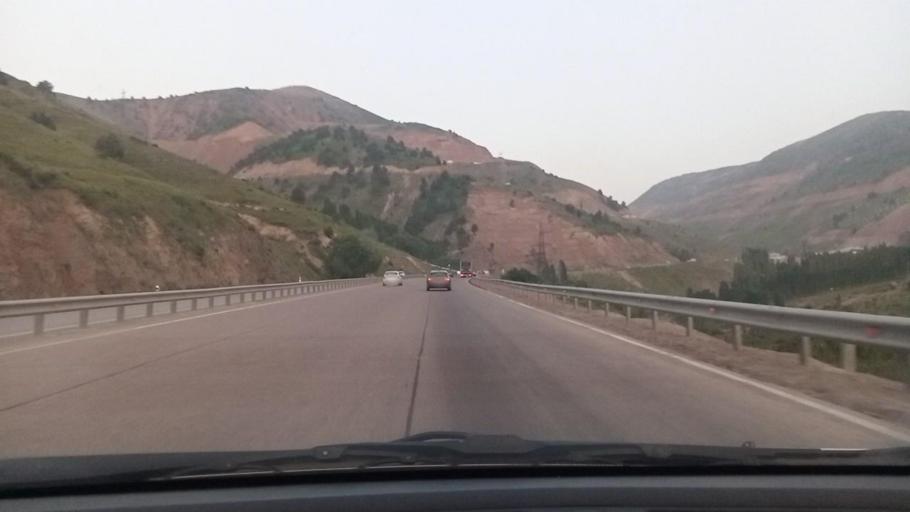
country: UZ
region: Toshkent
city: Angren
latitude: 41.1177
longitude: 70.4925
